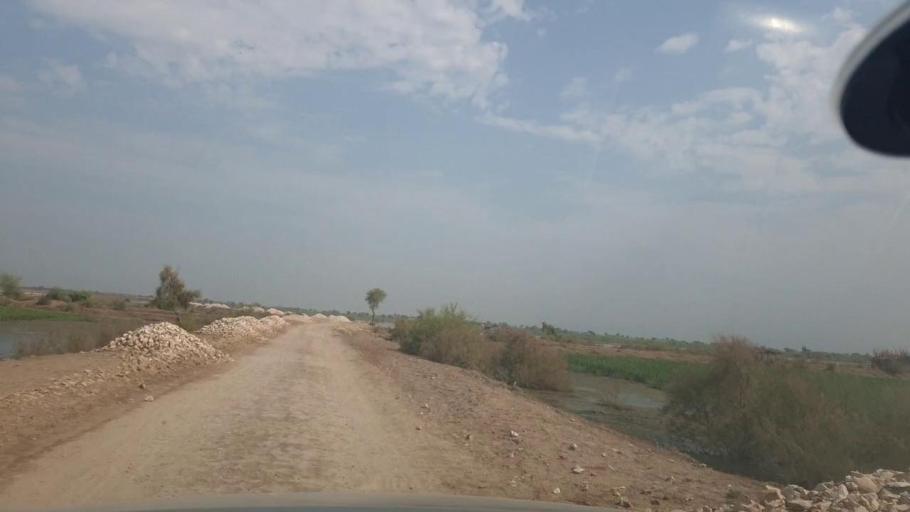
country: PK
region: Balochistan
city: Mehrabpur
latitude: 28.0781
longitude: 68.1012
